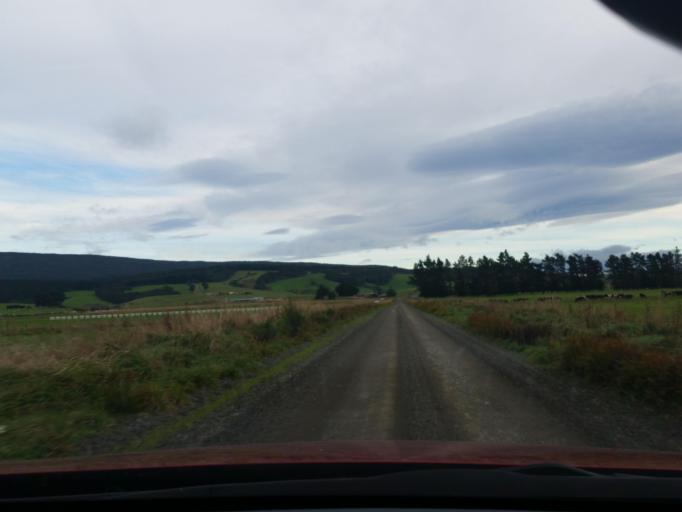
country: NZ
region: Southland
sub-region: Southland District
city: Riverton
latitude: -46.0997
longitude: 167.9543
